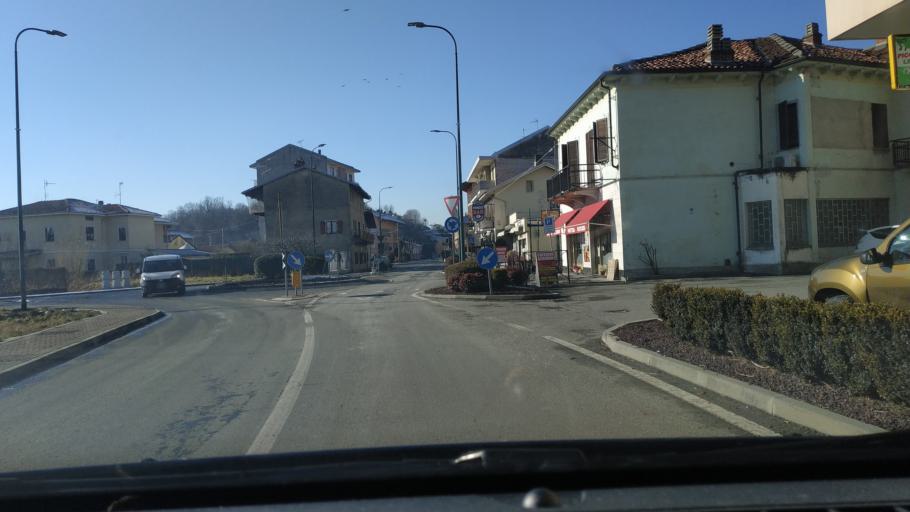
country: IT
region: Piedmont
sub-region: Provincia di Torino
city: Samone
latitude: 45.4508
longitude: 7.8485
